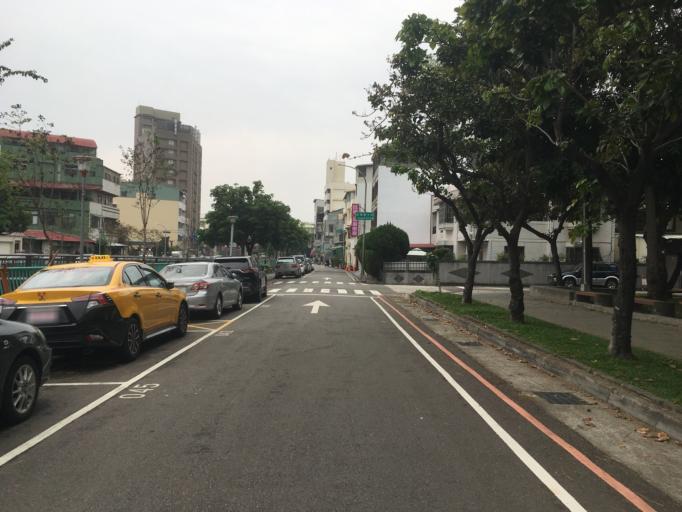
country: TW
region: Taiwan
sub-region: Taichung City
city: Taichung
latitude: 24.1736
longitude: 120.6923
